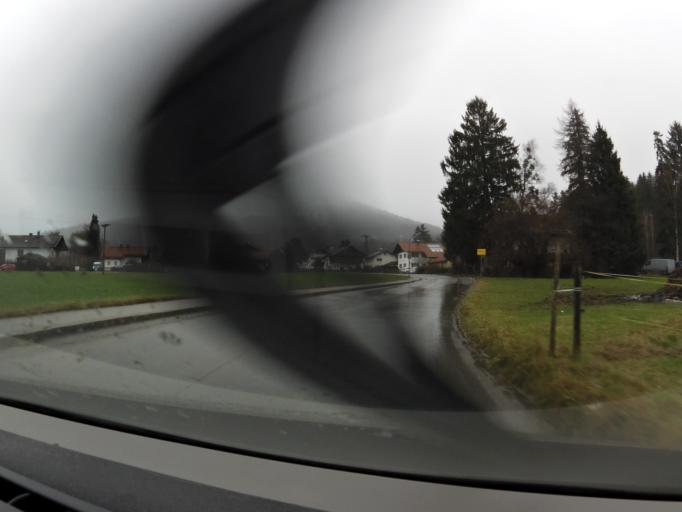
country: DE
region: Bavaria
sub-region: Upper Bavaria
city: Benediktbeuern
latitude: 47.7002
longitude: 11.4111
